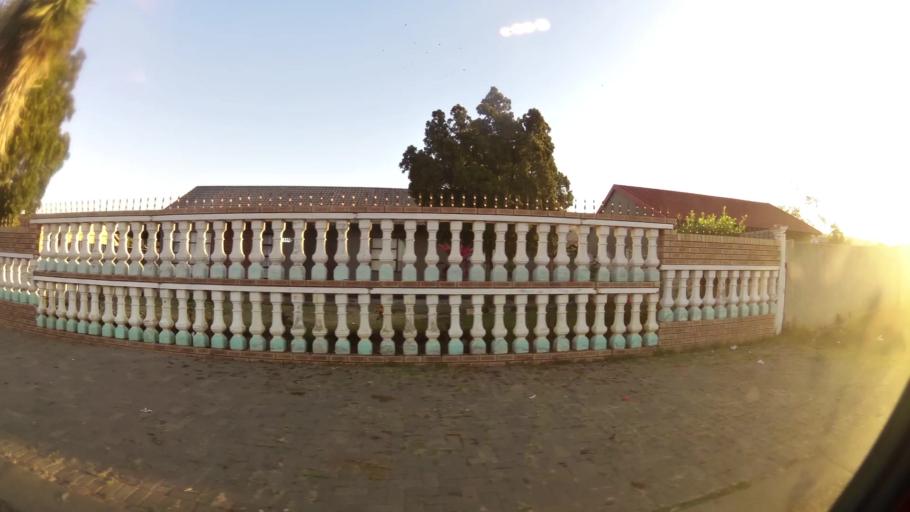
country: ZA
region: North-West
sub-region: Bojanala Platinum District Municipality
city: Rustenburg
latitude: -25.6372
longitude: 27.2047
